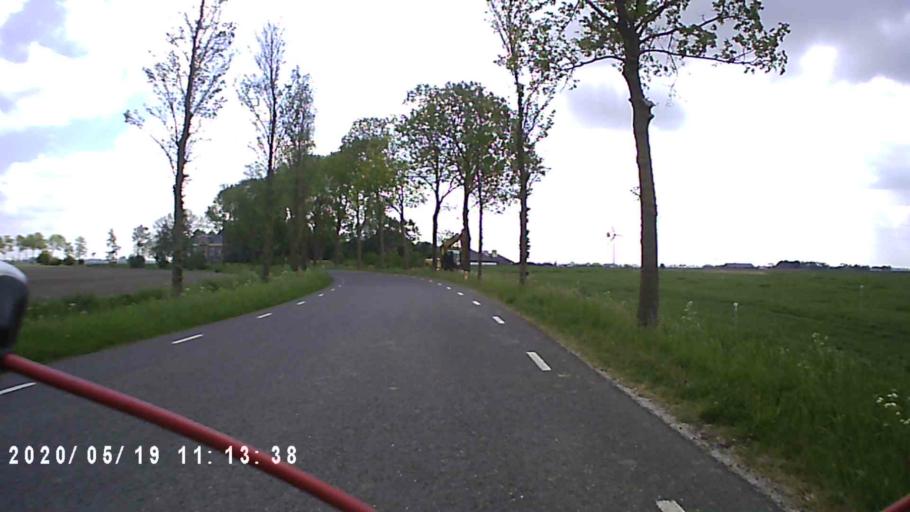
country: NL
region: Groningen
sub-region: Gemeente Zuidhorn
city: Grijpskerk
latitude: 53.2945
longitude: 6.3413
